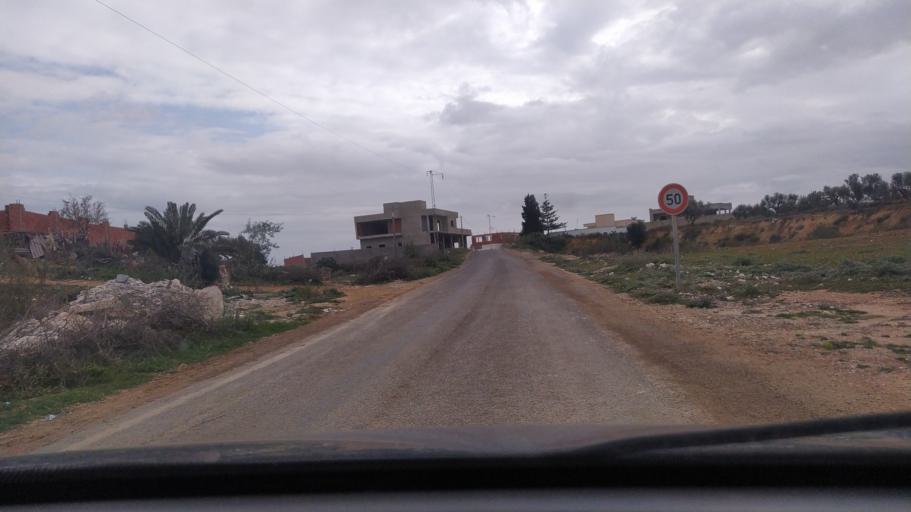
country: TN
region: Al Munastir
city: Sidi Bin Nur
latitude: 35.5157
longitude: 10.9663
